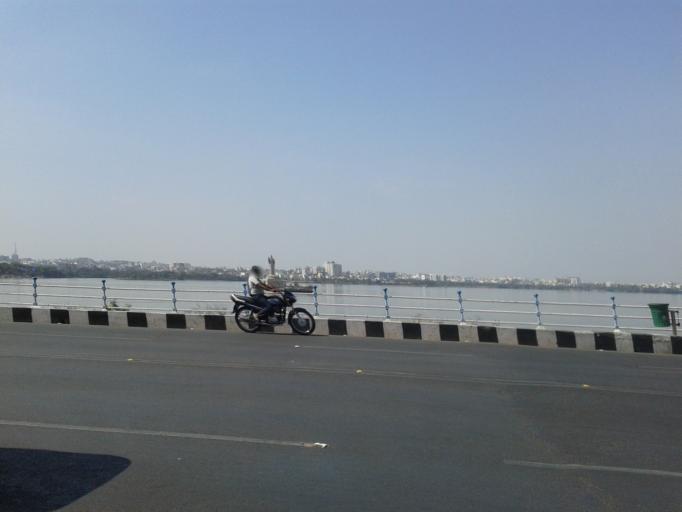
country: IN
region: Telangana
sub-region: Hyderabad
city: Hyderabad
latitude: 17.4142
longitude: 78.4789
